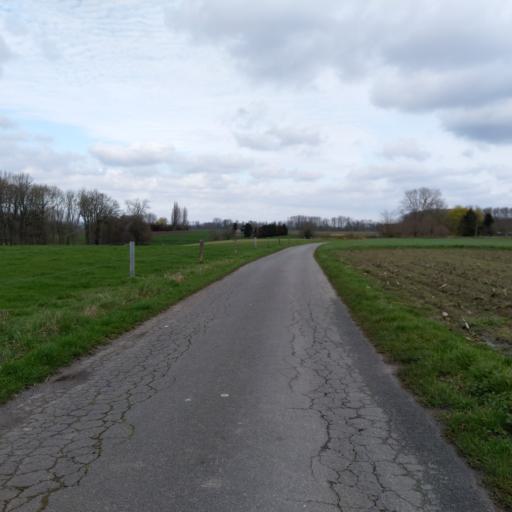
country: BE
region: Wallonia
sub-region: Province du Hainaut
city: Jurbise
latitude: 50.5243
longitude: 3.9839
